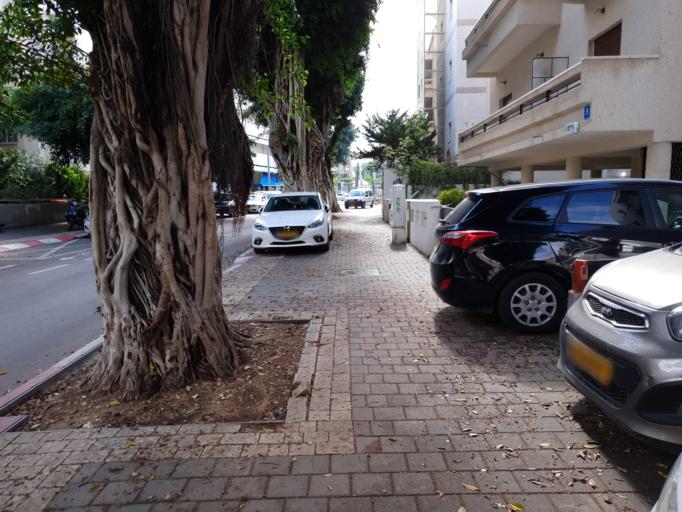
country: IL
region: Tel Aviv
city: Tel Aviv
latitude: 32.0789
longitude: 34.7749
